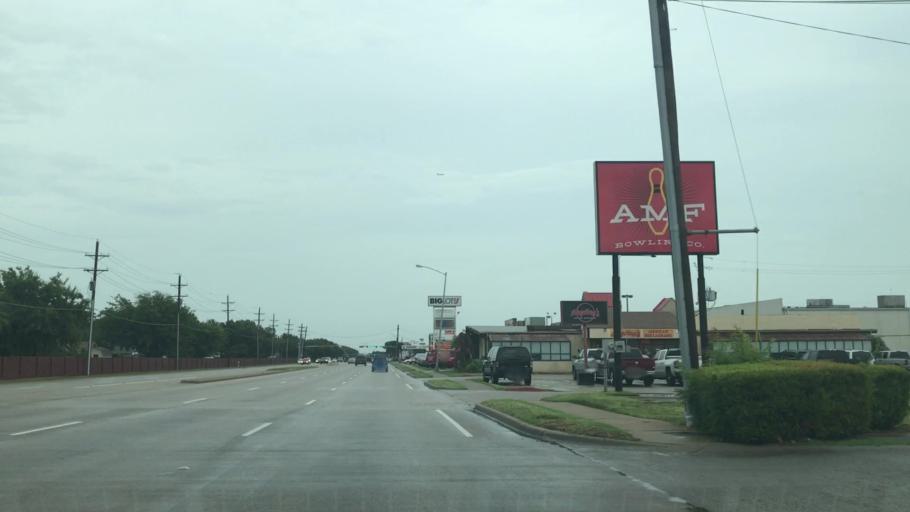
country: US
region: Texas
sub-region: Denton County
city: Lewisville
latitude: 33.0421
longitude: -97.0310
